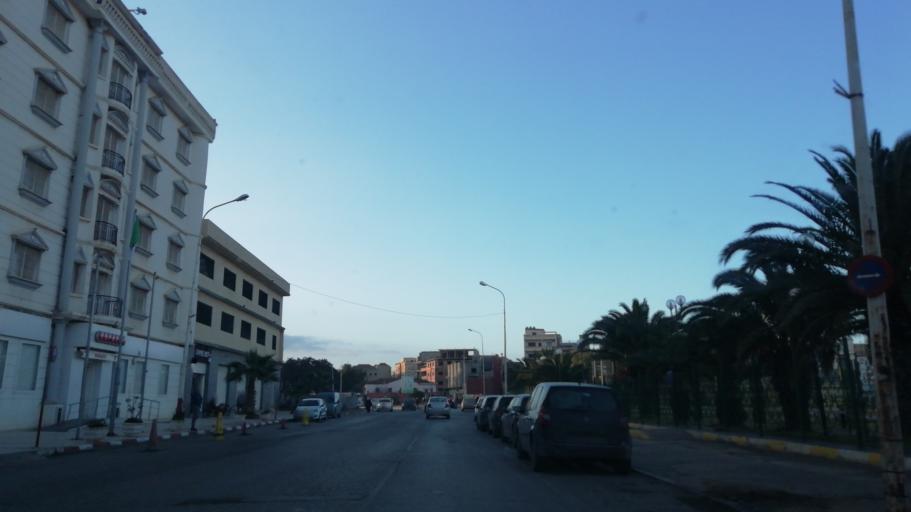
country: DZ
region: Oran
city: Oran
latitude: 35.6692
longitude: -0.6590
